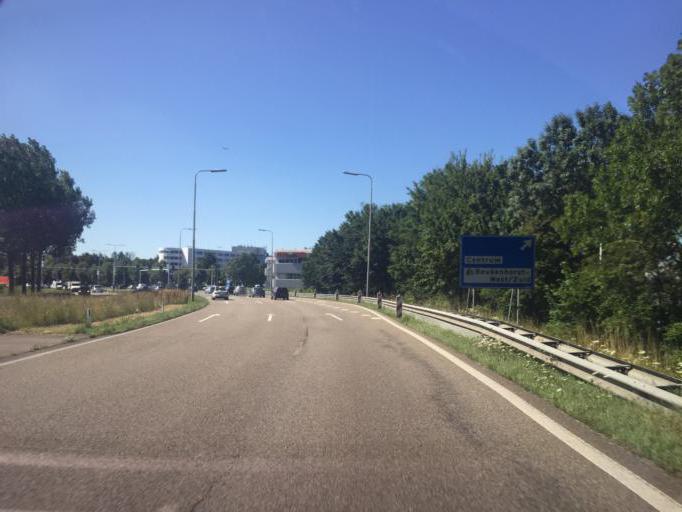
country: NL
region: North Holland
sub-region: Gemeente Haarlemmermeer
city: Hoofddorp
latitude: 52.2989
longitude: 4.7095
